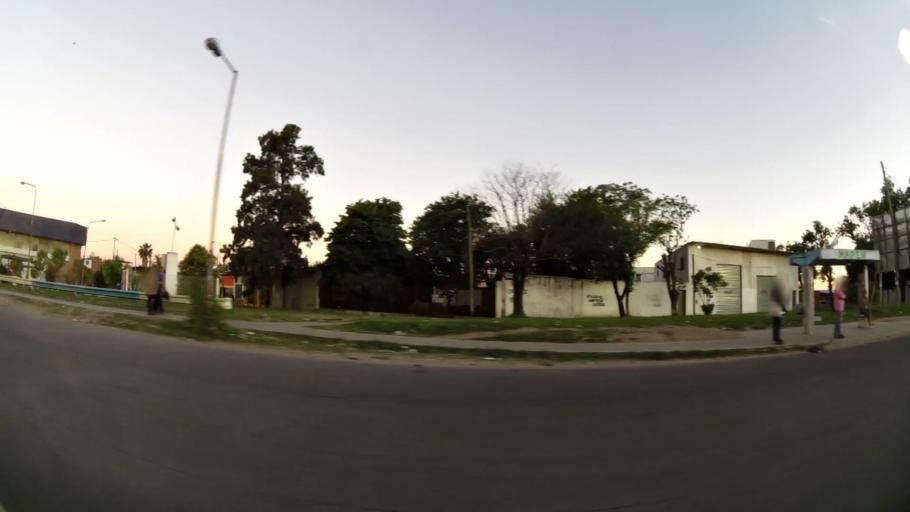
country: AR
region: Buenos Aires
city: San Justo
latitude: -34.7252
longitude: -58.5987
